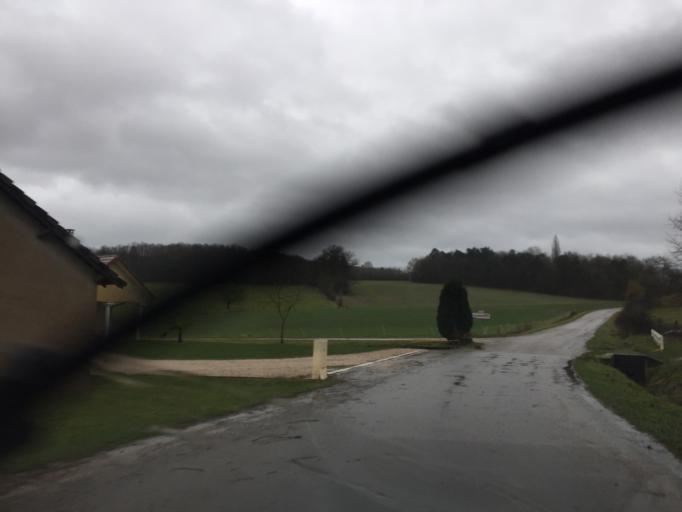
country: FR
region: Franche-Comte
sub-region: Departement du Jura
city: Dole
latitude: 47.1564
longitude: 5.5177
